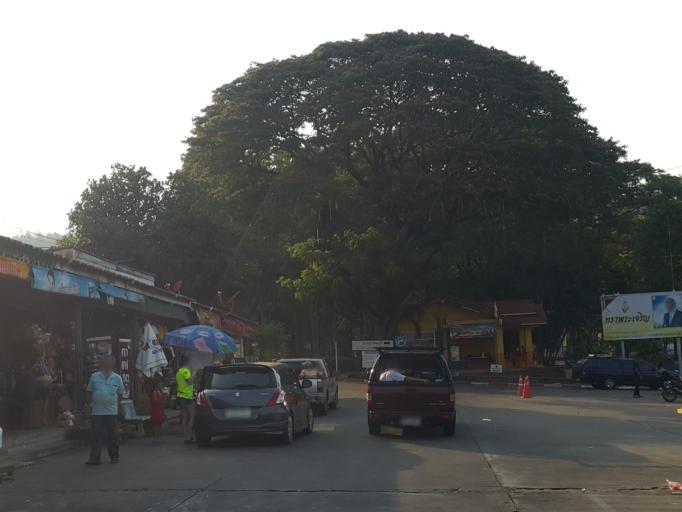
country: TH
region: Kanchanaburi
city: Si Sawat
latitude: 14.3835
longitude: 99.1360
